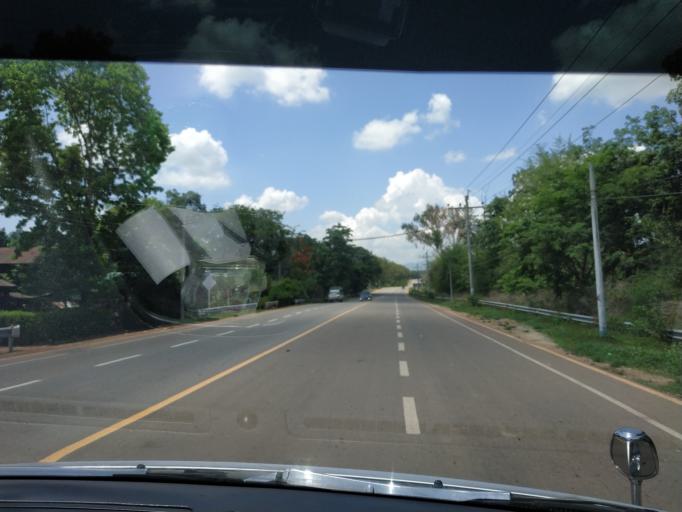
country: MM
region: Mon
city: Kyaikto
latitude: 17.3152
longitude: 97.0187
